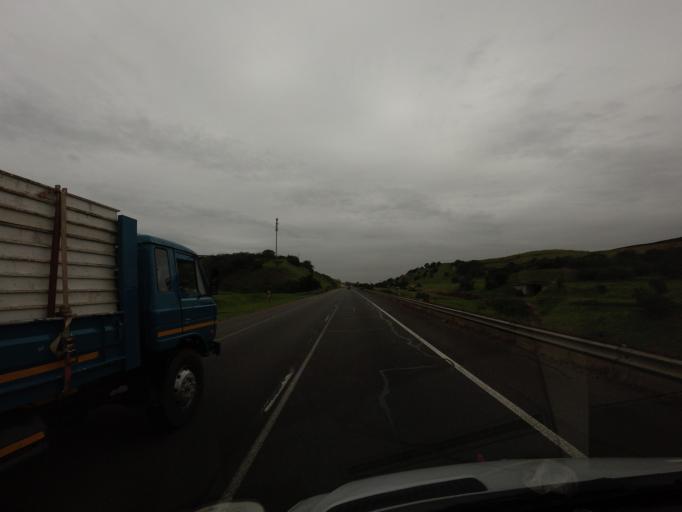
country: ZA
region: KwaZulu-Natal
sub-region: eThekwini Metropolitan Municipality
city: Durban
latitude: -29.7036
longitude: 31.0695
